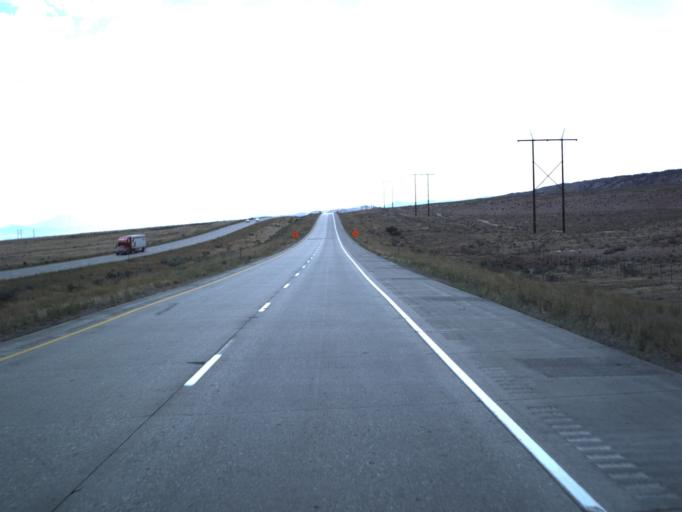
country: US
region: Utah
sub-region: Sevier County
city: Richfield
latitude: 38.8319
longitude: -112.0342
